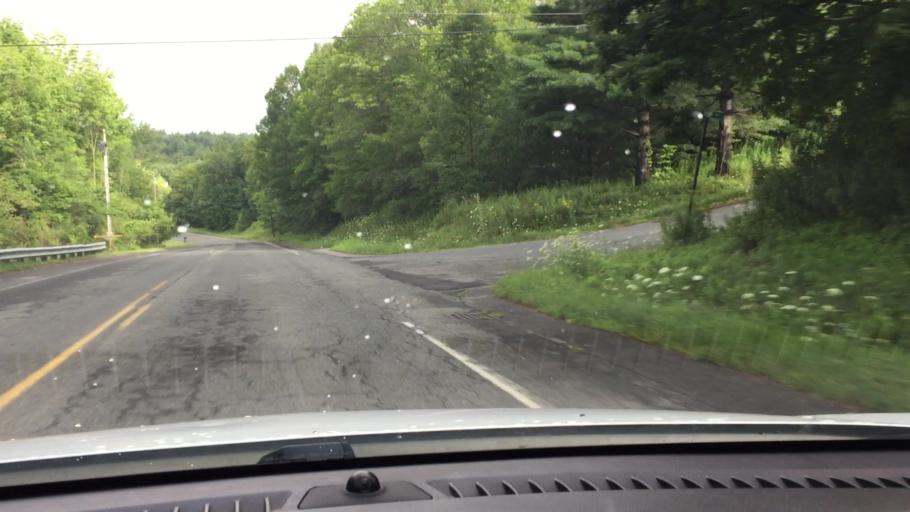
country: US
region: Massachusetts
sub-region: Berkshire County
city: Hinsdale
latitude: 42.4322
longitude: -73.0179
